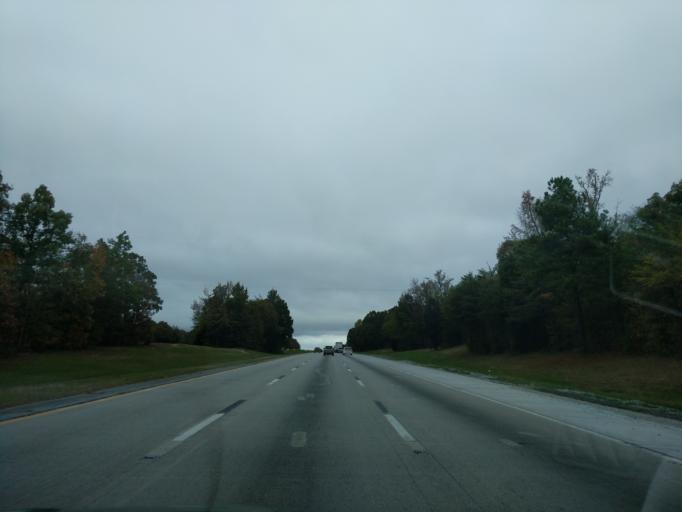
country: US
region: North Carolina
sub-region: Guilford County
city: Jamestown
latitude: 35.9515
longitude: -79.8986
